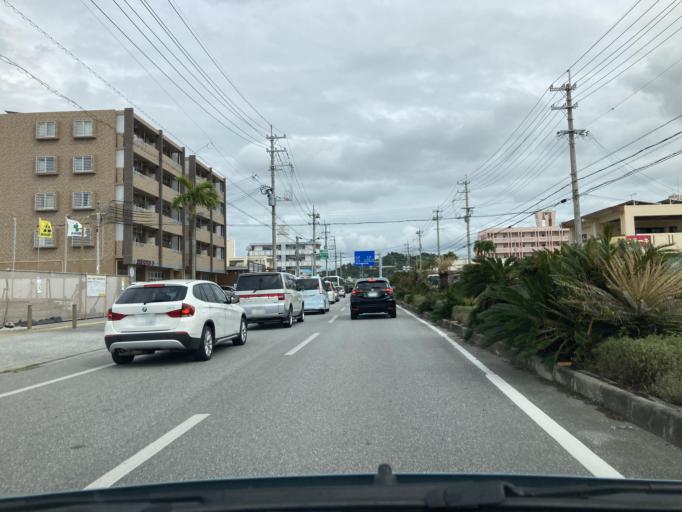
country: JP
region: Okinawa
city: Tomigusuku
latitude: 26.1617
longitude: 127.6673
